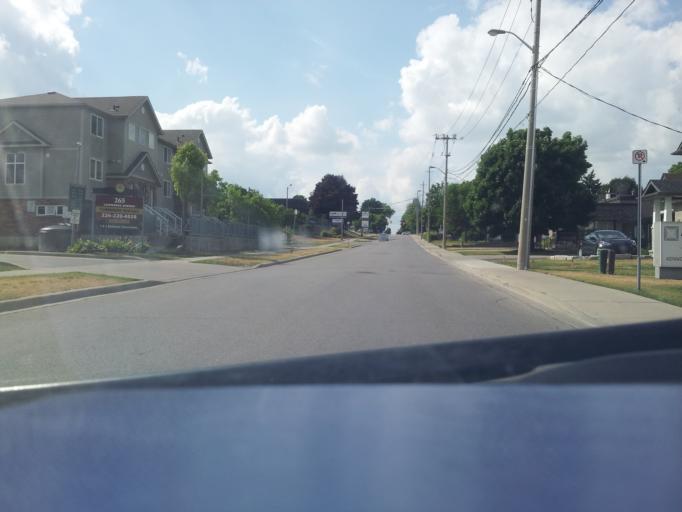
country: CA
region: Ontario
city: Kitchener
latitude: 43.4401
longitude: -80.5123
